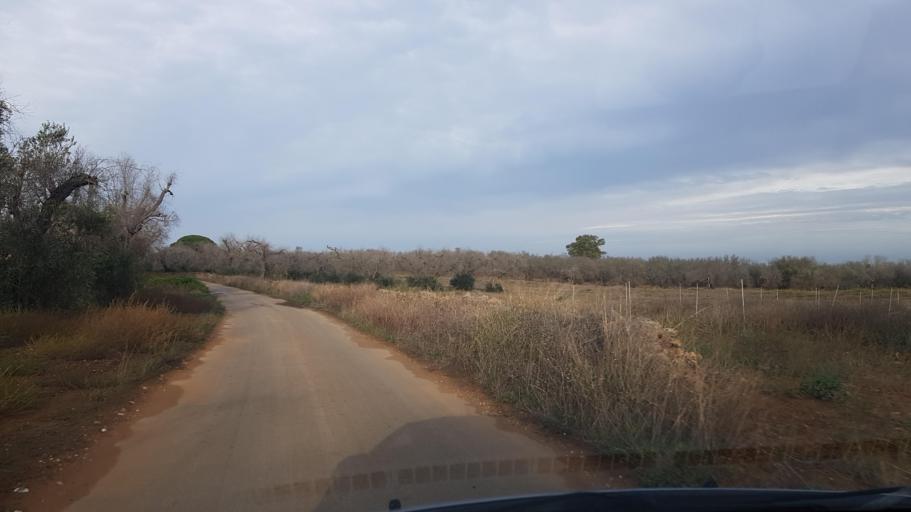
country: IT
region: Apulia
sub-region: Provincia di Brindisi
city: Torchiarolo
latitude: 40.4955
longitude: 18.0800
